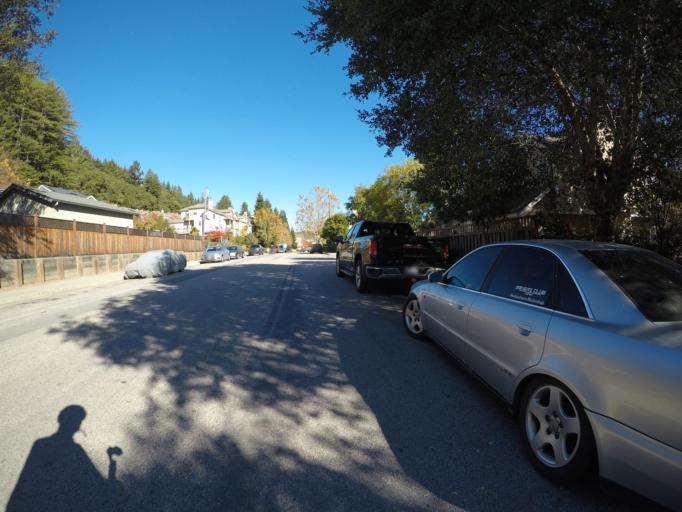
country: US
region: California
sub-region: Santa Cruz County
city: Scotts Valley
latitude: 37.0504
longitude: -122.0170
